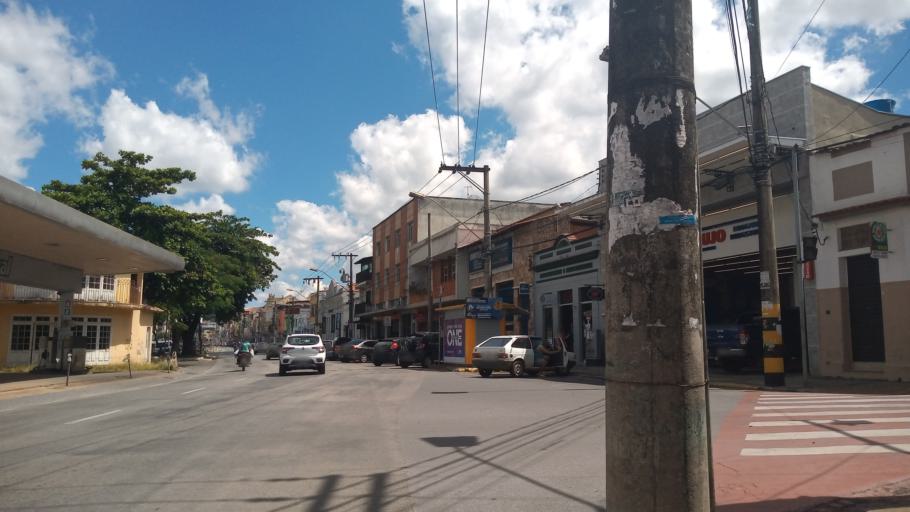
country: BR
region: Minas Gerais
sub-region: Sao Joao Del Rei
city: Sao Joao del Rei
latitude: -21.1309
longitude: -44.2542
